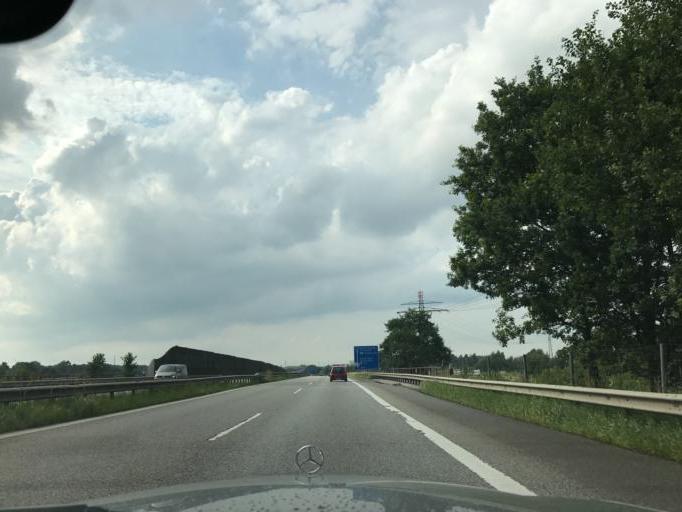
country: DE
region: Hamburg
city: Rothenburgsort
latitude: 53.4966
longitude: 10.0960
